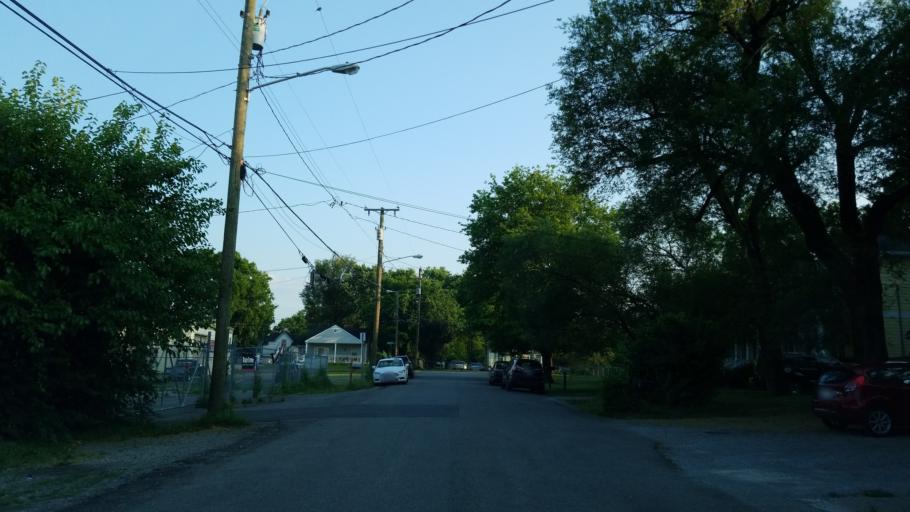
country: US
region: Tennessee
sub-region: Davidson County
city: Nashville
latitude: 36.1402
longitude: -86.7651
